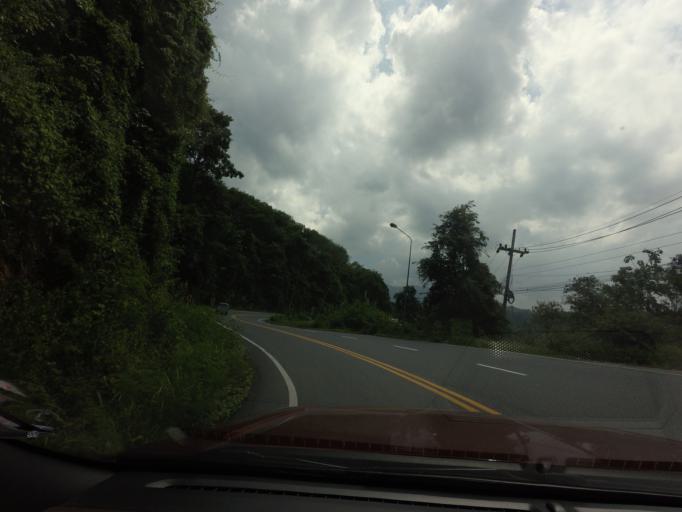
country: TH
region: Yala
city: Than To
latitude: 6.0396
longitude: 101.2099
